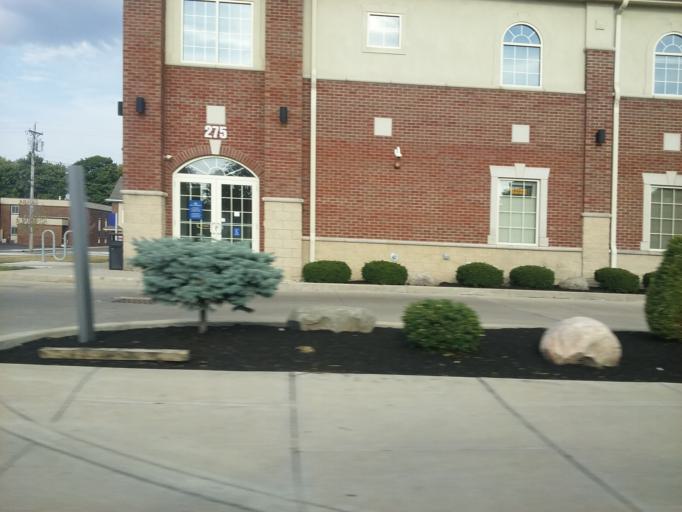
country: US
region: Ohio
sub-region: Wood County
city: Bowling Green
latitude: 41.3717
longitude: -83.6503
